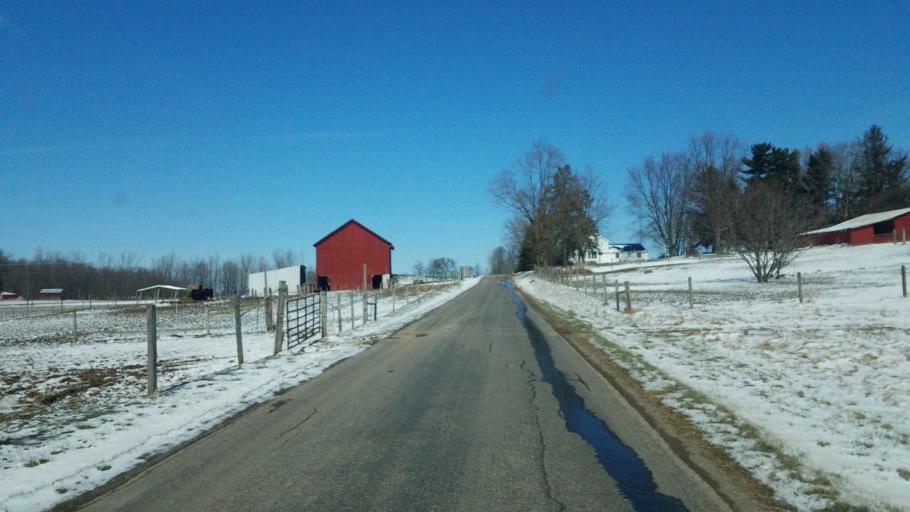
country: US
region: Ohio
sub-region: Richland County
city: Lexington
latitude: 40.5849
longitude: -82.6183
